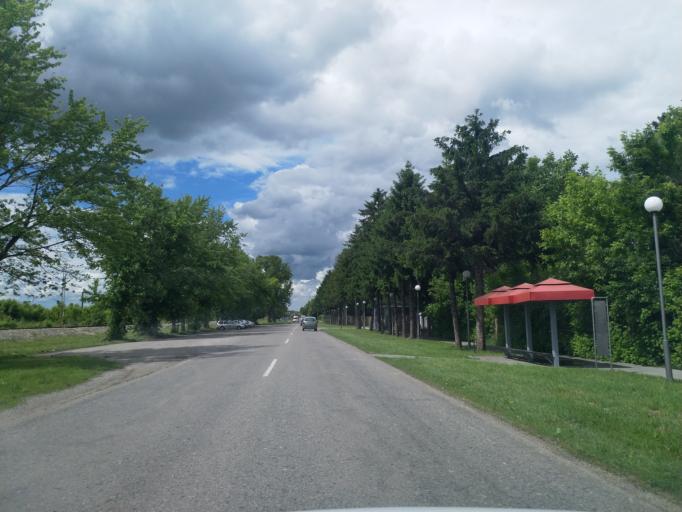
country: RS
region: Central Serbia
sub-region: Pomoravski Okrug
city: Cuprija
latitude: 43.9038
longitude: 21.3789
